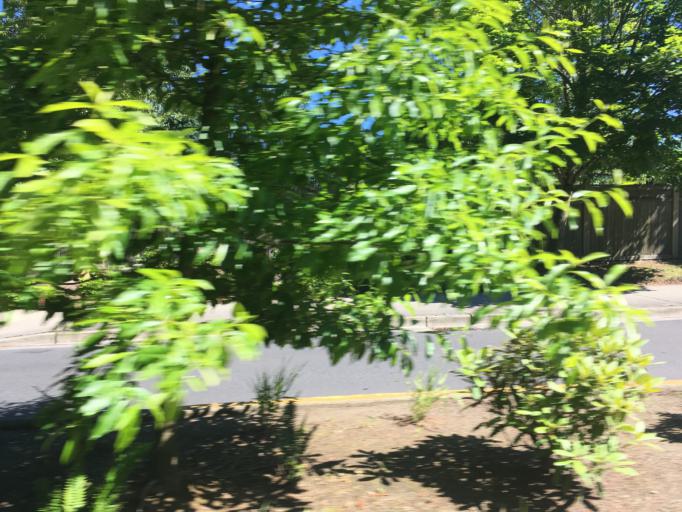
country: US
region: Washington
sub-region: King County
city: Redmond
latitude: 47.6315
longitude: -122.1305
